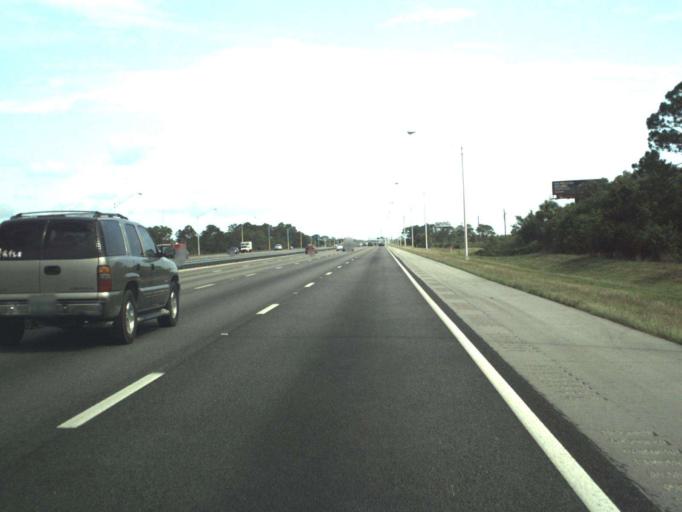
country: US
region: Florida
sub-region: Saint Lucie County
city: Lakewood Park
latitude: 27.4906
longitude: -80.4373
